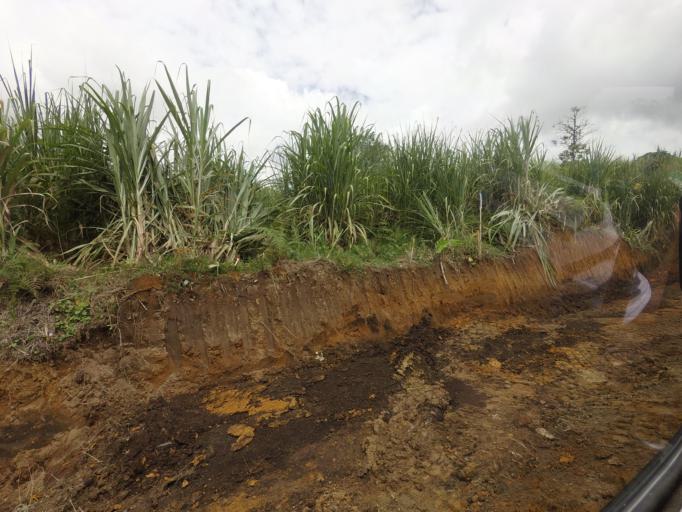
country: CO
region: Huila
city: Isnos
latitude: 1.9556
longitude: -76.2891
